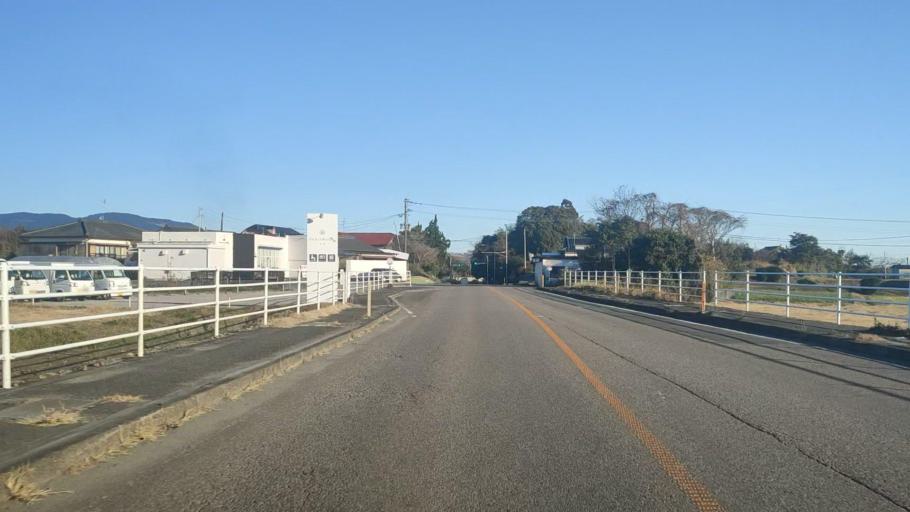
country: JP
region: Miyazaki
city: Takanabe
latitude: 32.2326
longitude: 131.5485
